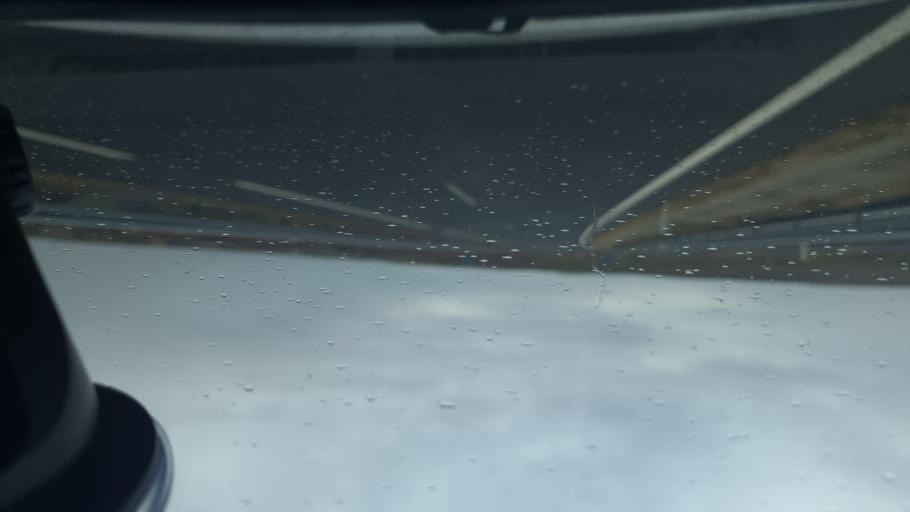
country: ES
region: Castille and Leon
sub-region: Provincia de Segovia
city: Roda de Eresma
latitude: 41.0184
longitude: -4.1778
